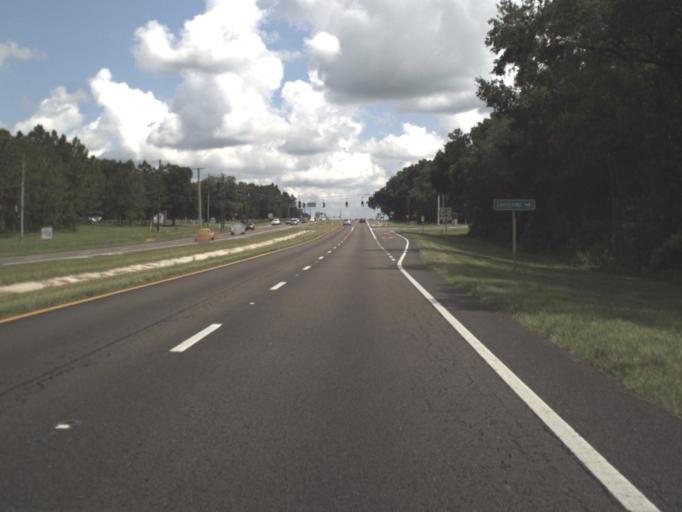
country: US
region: Florida
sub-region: Pasco County
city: Dade City
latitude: 28.3221
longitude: -82.1875
